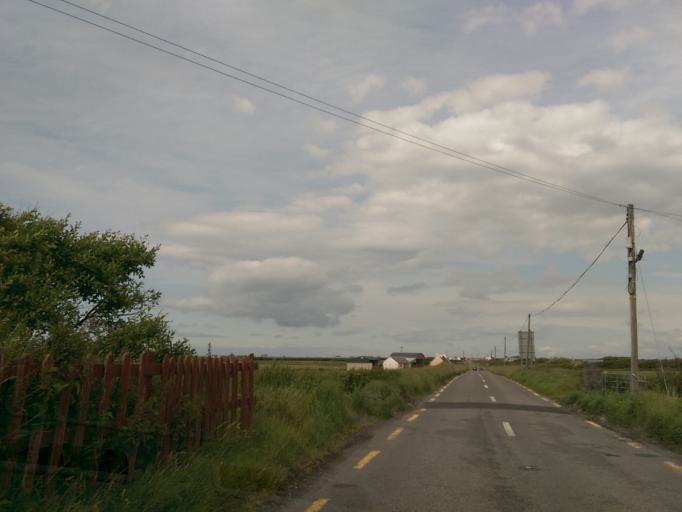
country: IE
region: Munster
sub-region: An Clar
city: Kilrush
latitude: 52.7464
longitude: -9.4796
